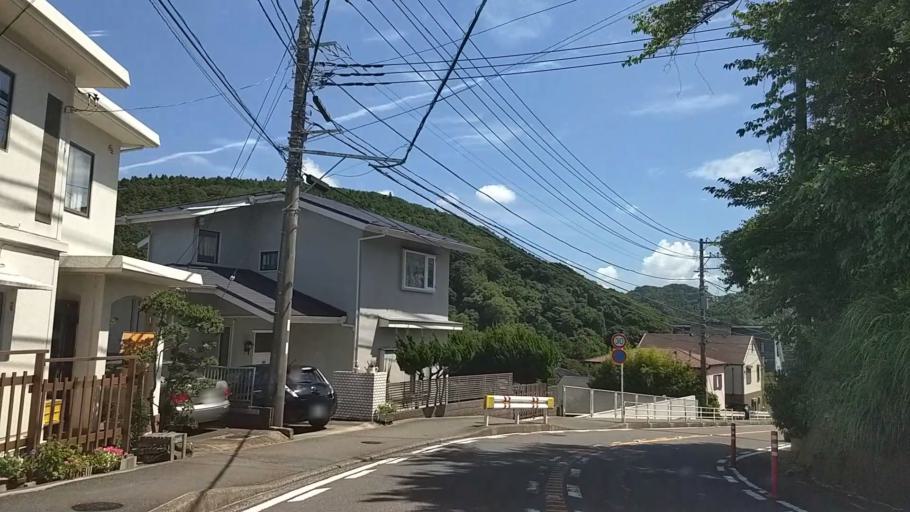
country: JP
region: Kanagawa
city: Zushi
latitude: 35.2880
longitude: 139.5916
